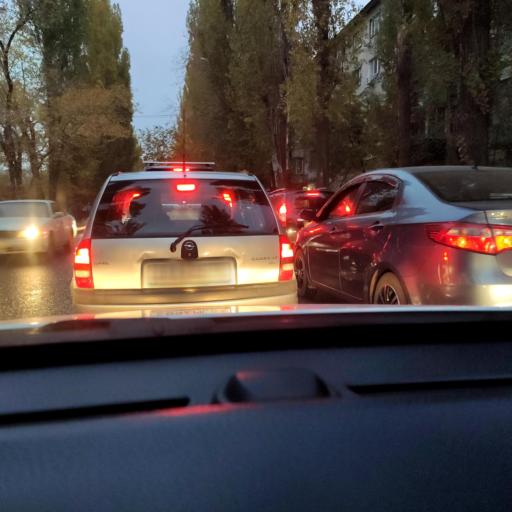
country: RU
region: Voronezj
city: Voronezh
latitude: 51.6842
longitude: 39.2567
